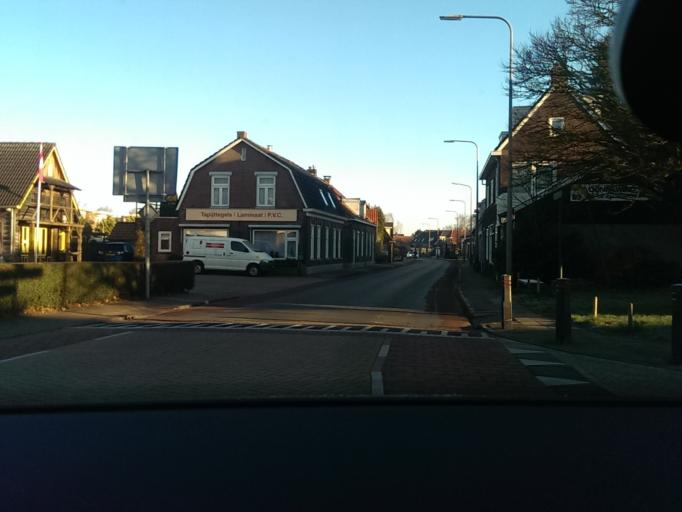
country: NL
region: Overijssel
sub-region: Gemeente Twenterand
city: Den Ham
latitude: 52.5205
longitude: 6.4254
